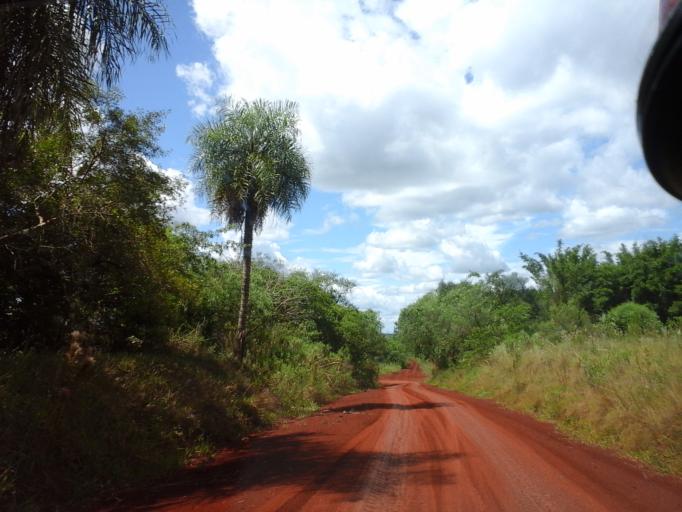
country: AR
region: Misiones
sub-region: Departamento de Apostoles
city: Apostoles
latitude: -27.9767
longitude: -55.7738
